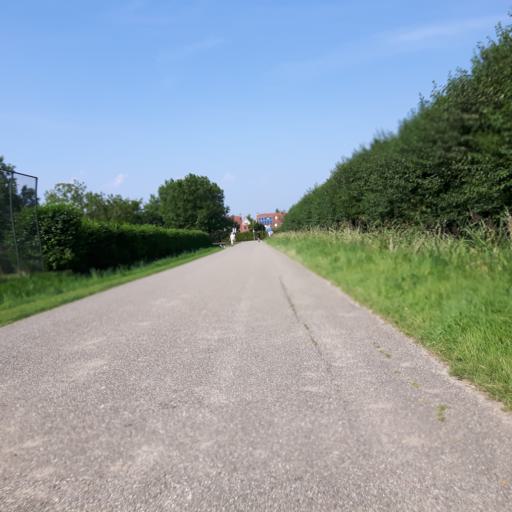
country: NL
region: Zeeland
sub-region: Gemeente Goes
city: Goes
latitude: 51.4889
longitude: 3.9130
